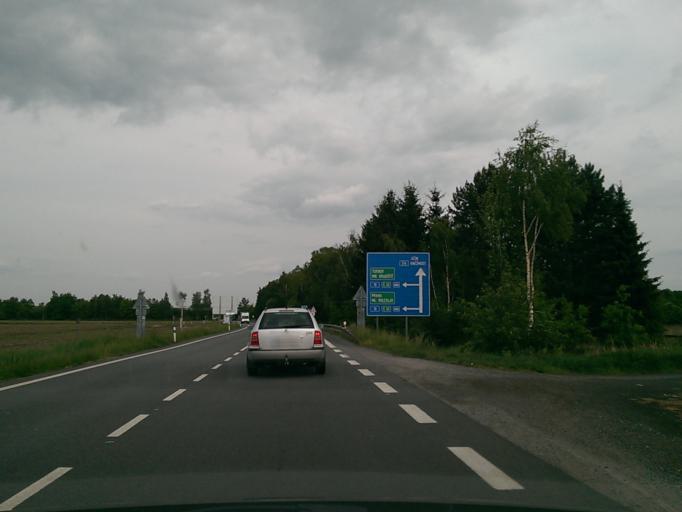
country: CZ
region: Central Bohemia
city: Bakov nad Jizerou
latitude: 50.4830
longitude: 14.9598
